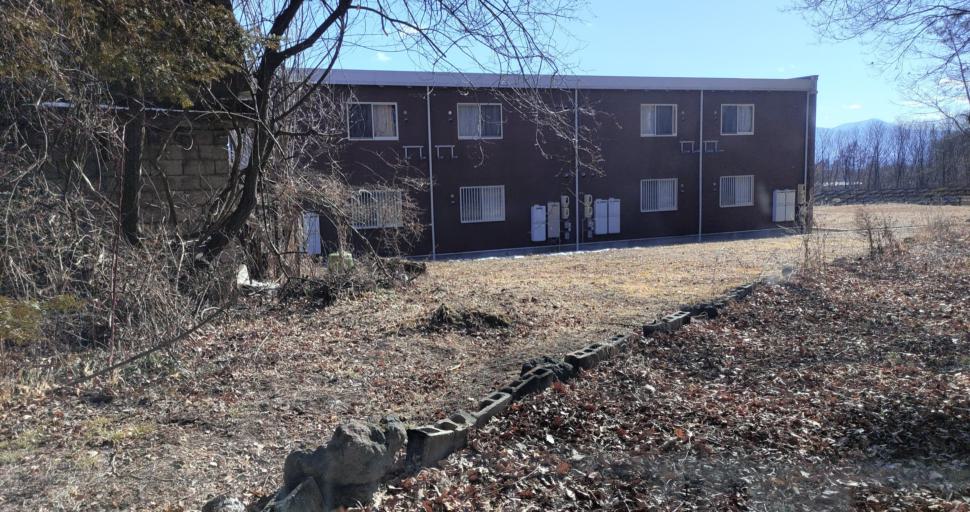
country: JP
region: Nagano
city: Komoro
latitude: 36.3330
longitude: 138.5146
